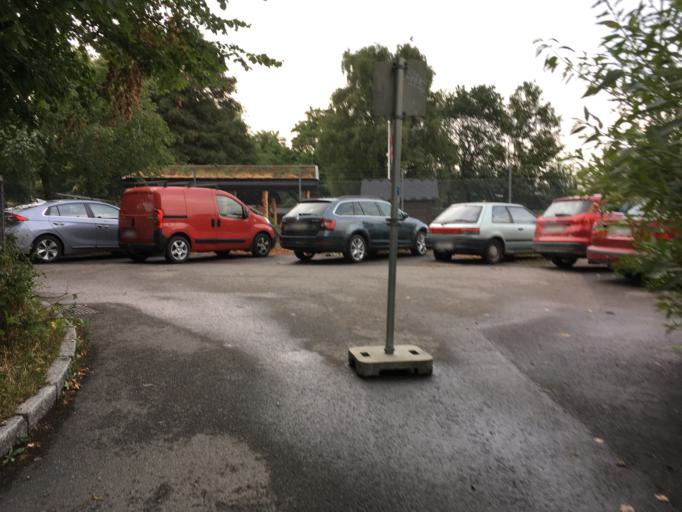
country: NO
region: Oslo
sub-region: Oslo
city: Oslo
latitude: 59.9127
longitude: 10.7855
